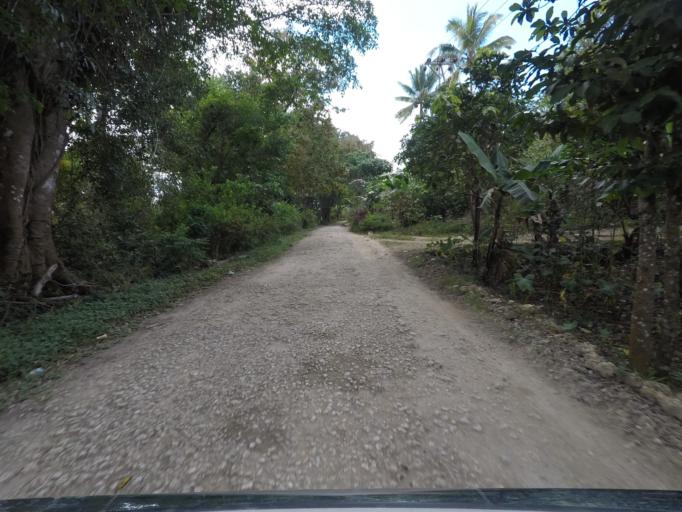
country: TL
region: Baucau
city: Venilale
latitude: -8.6387
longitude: 126.3826
